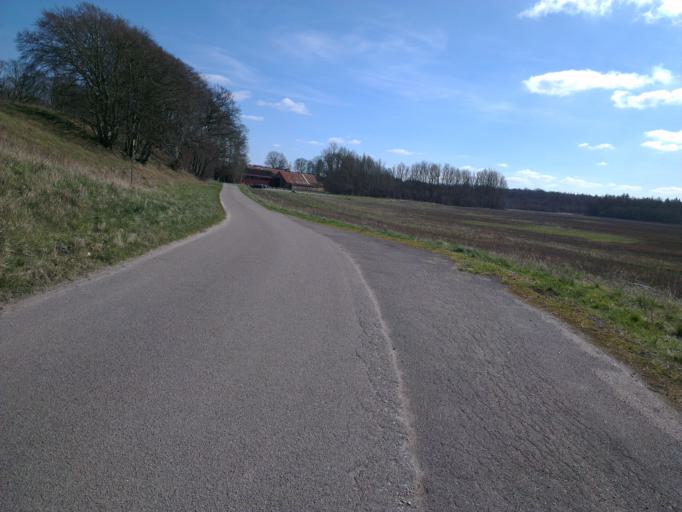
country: DK
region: Capital Region
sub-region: Frederikssund Kommune
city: Jaegerspris
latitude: 55.8932
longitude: 11.9874
